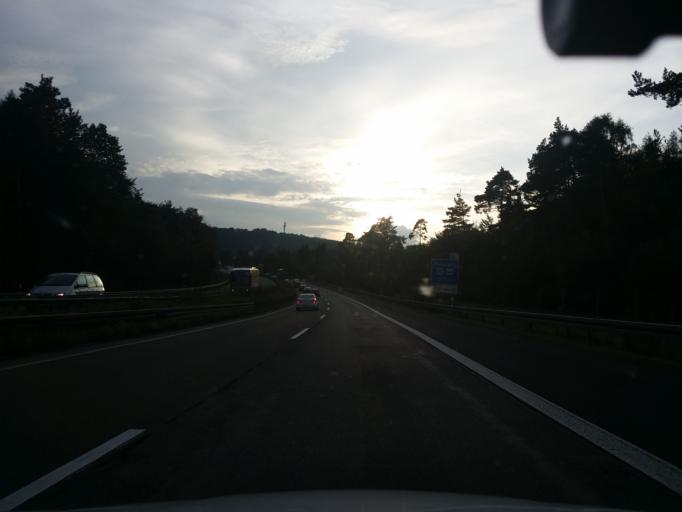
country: DE
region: Hesse
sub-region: Regierungsbezirk Kassel
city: Oberaula
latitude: 50.7975
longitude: 9.4875
